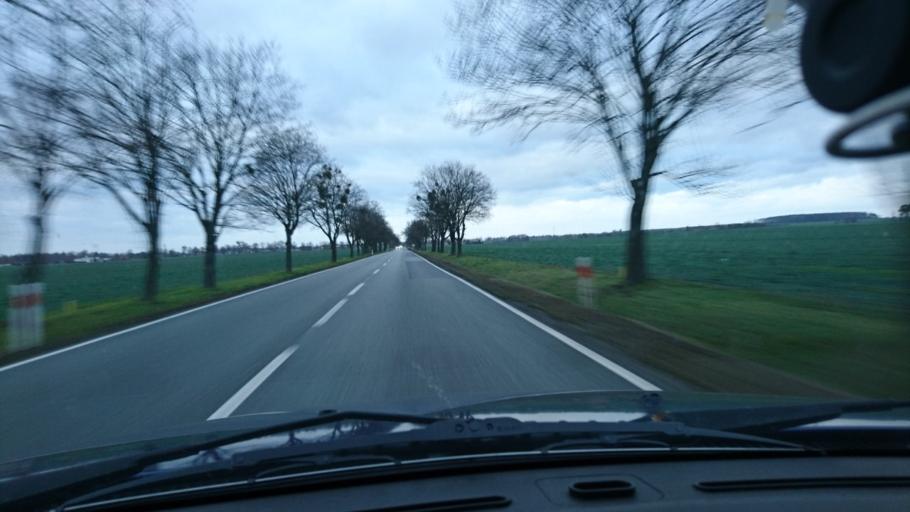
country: PL
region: Opole Voivodeship
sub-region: Powiat kluczborski
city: Byczyna
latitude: 51.0723
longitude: 18.2028
